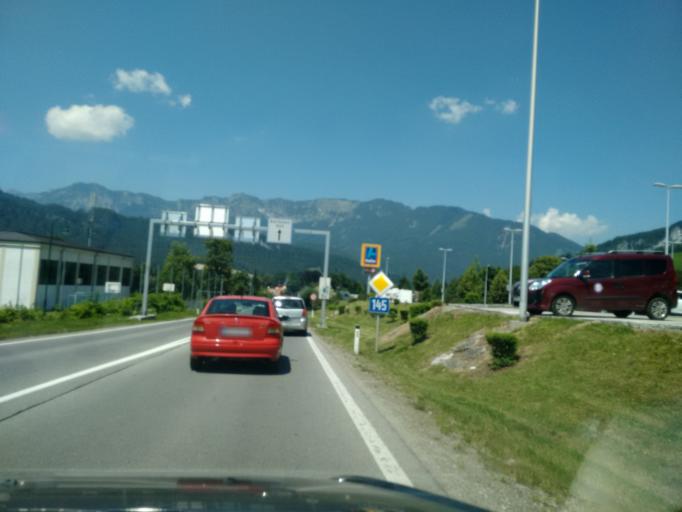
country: AT
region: Upper Austria
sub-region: Politischer Bezirk Gmunden
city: Bad Goisern
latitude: 47.6412
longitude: 13.6202
